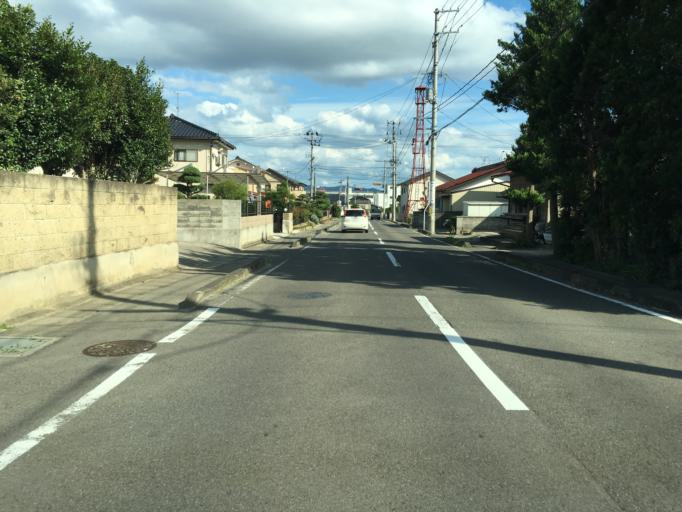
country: JP
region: Fukushima
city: Fukushima-shi
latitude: 37.7697
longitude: 140.4199
